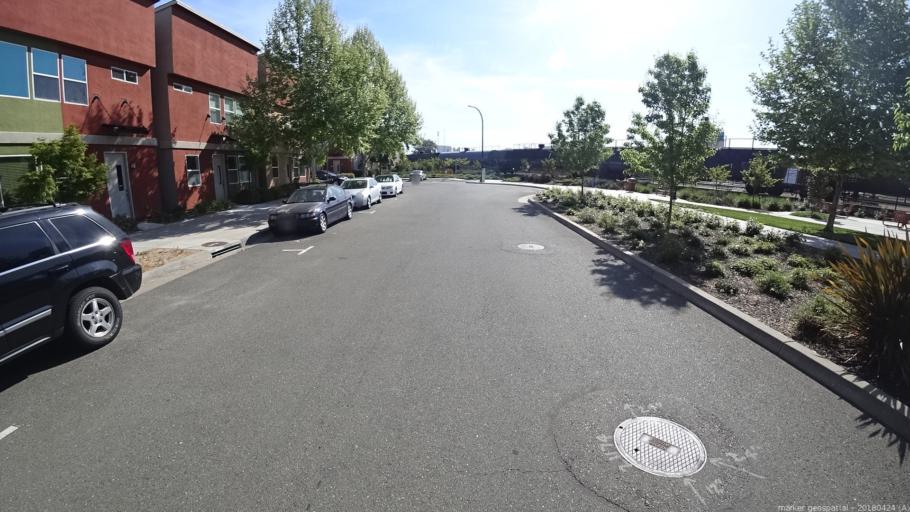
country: US
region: California
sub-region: Yolo County
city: West Sacramento
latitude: 38.5781
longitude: -121.5191
